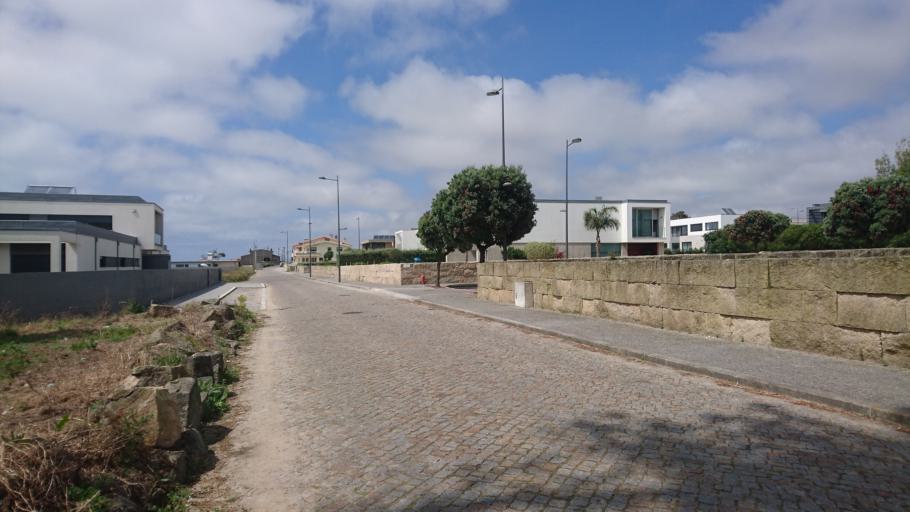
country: PT
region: Porto
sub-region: Matosinhos
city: Lavra
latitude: 41.2771
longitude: -8.7238
